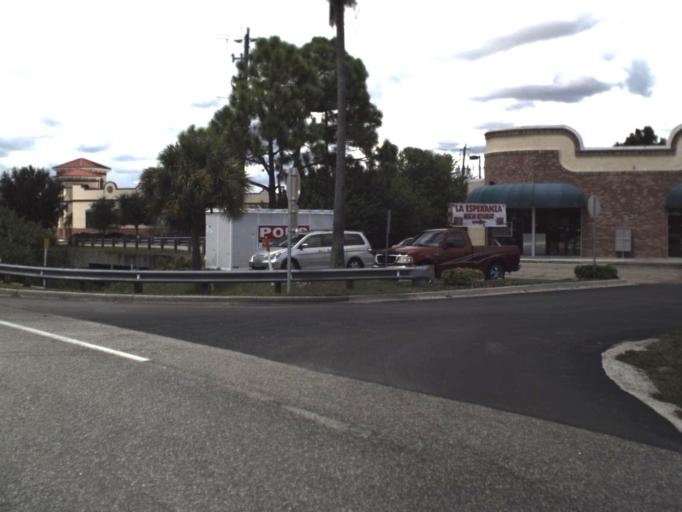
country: US
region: Florida
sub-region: Charlotte County
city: Port Charlotte
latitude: 27.0055
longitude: -82.1310
